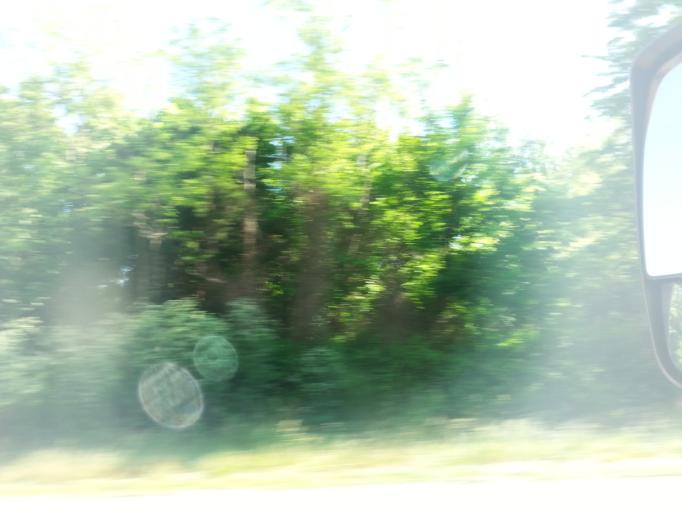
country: US
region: Kentucky
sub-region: Shelby County
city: Shelbyville
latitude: 38.1793
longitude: -85.1762
